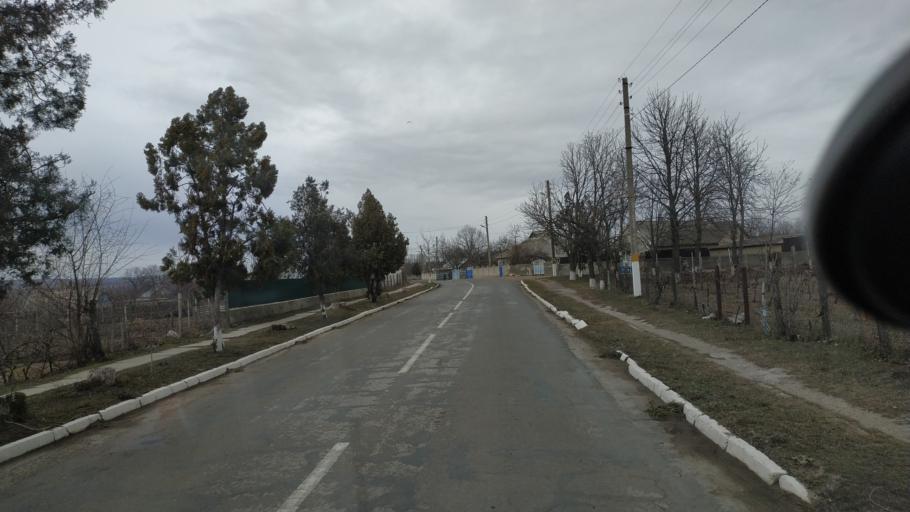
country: MD
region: Telenesti
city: Cocieri
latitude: 47.3035
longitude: 29.1131
